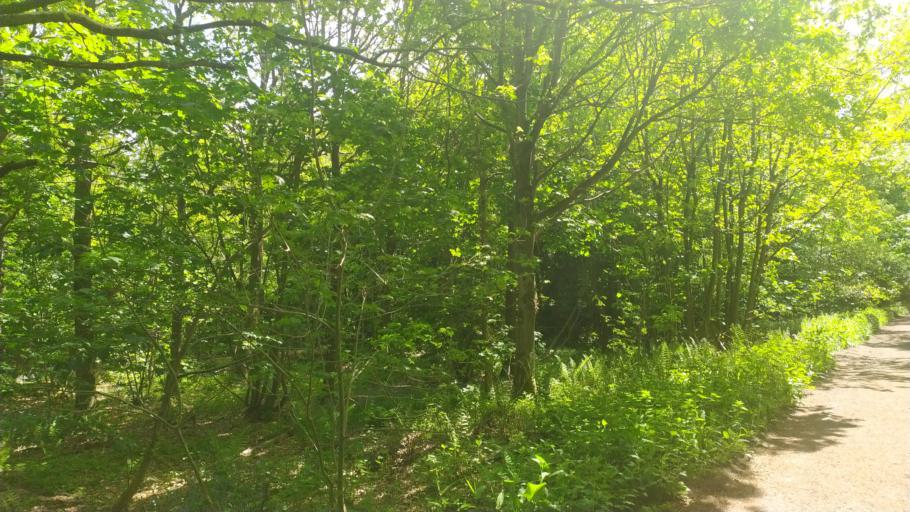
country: GB
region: England
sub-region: City and Borough of Leeds
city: Shadwell
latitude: 53.8918
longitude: -1.5113
